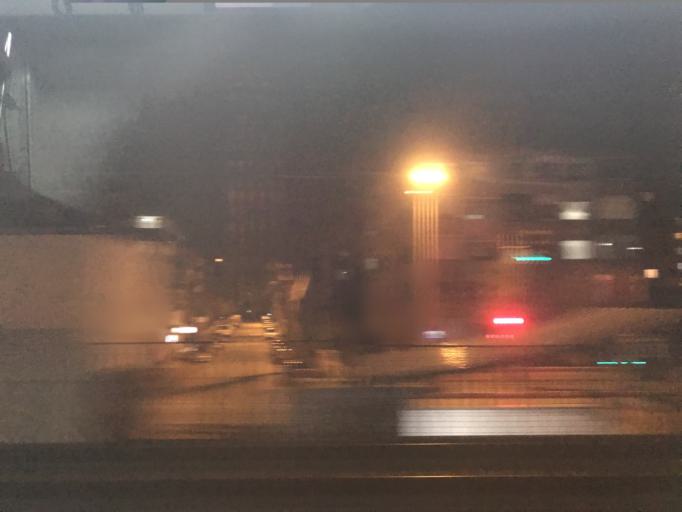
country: TR
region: Istanbul
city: Maltepe
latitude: 40.9032
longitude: 29.1643
